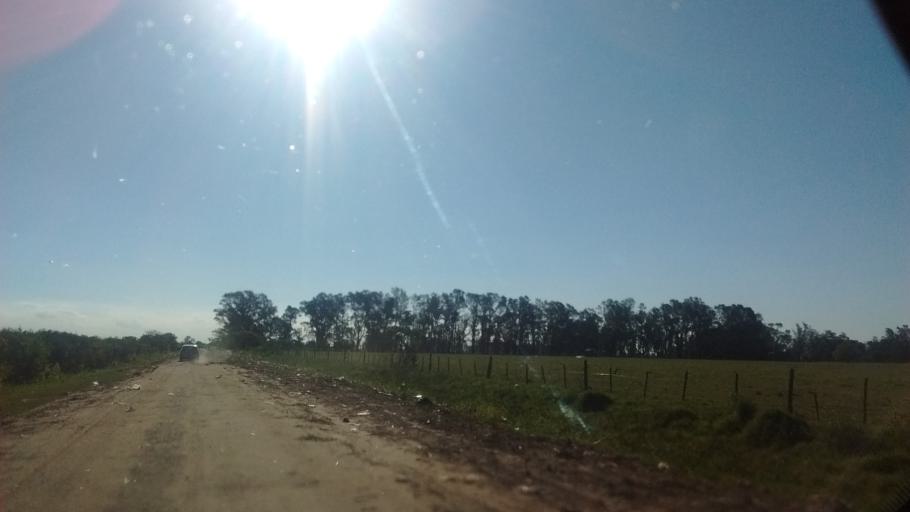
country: AR
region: Santa Fe
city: Funes
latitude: -32.8935
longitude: -60.8007
